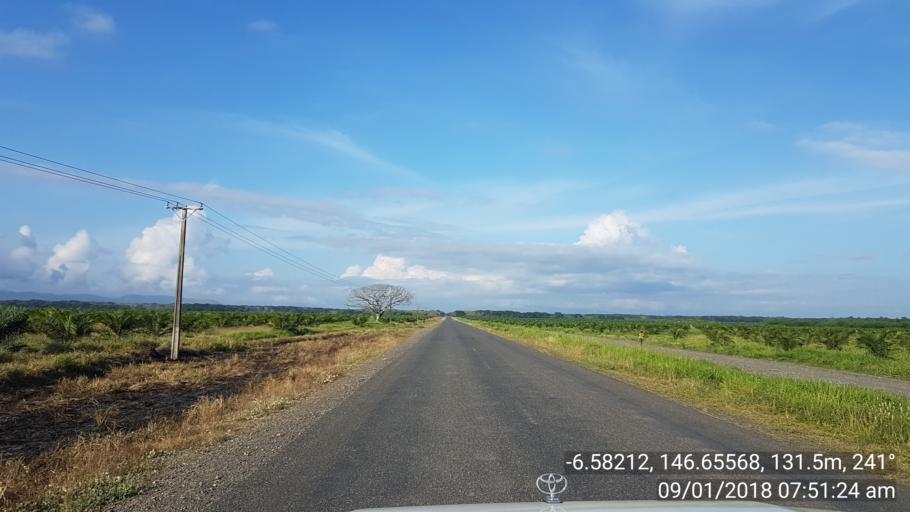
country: PG
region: Morobe
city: Lae
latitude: -6.5822
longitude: 146.6556
